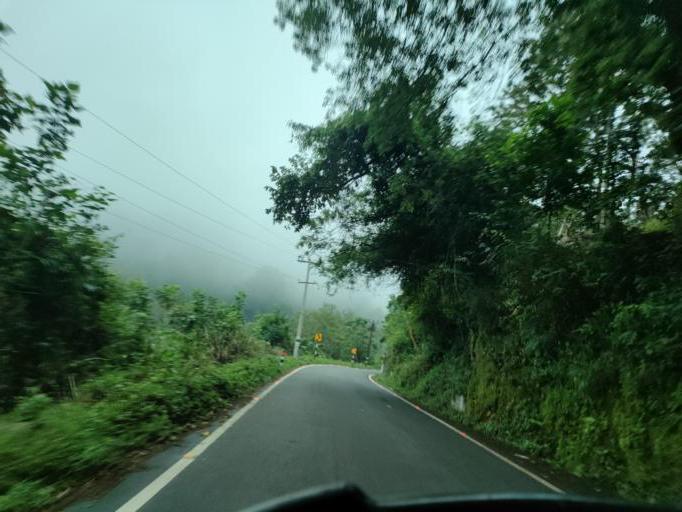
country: IN
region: Tamil Nadu
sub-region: Dindigul
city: Ayakudi
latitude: 10.3554
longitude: 77.5593
